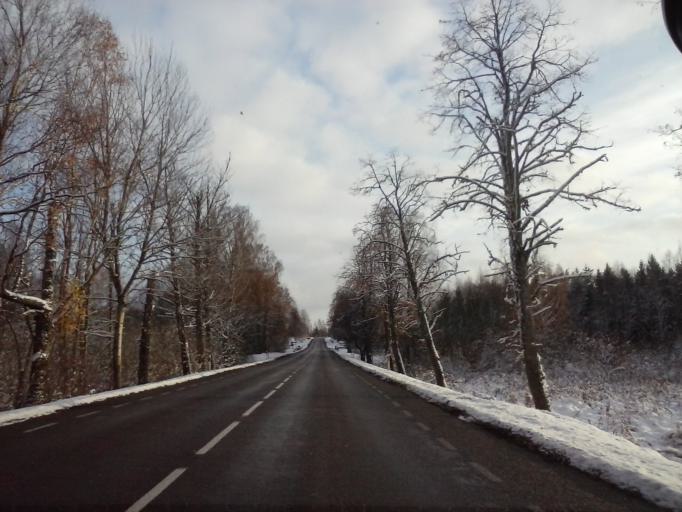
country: EE
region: Tartu
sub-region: Tartu linn
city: Tartu
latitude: 58.3516
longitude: 26.9089
